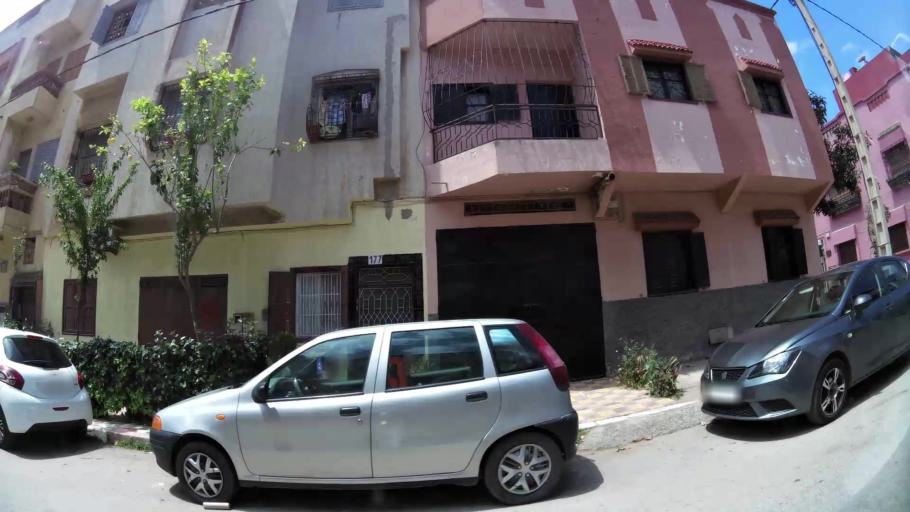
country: MA
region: Gharb-Chrarda-Beni Hssen
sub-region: Kenitra Province
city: Kenitra
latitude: 34.2731
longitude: -6.5997
